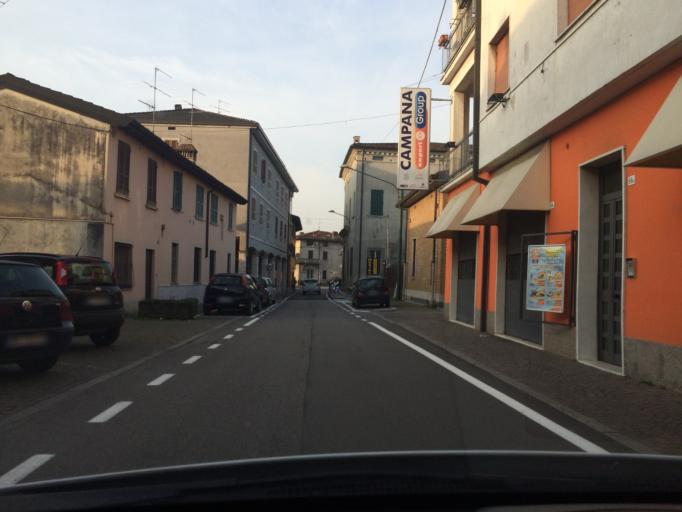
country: IT
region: Lombardy
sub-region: Provincia di Brescia
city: Flero
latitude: 45.4870
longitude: 10.1745
